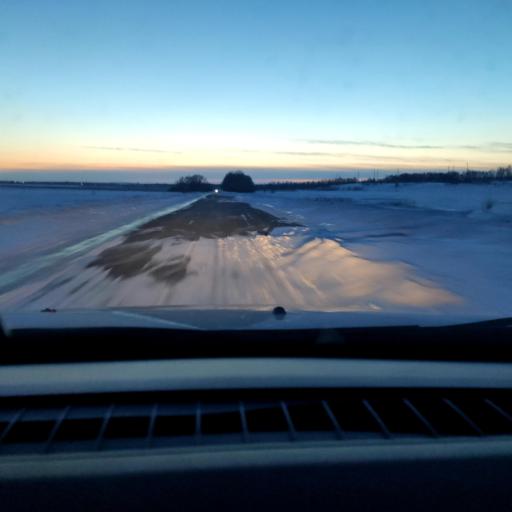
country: RU
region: Samara
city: Georgiyevka
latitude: 53.3364
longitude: 50.9388
